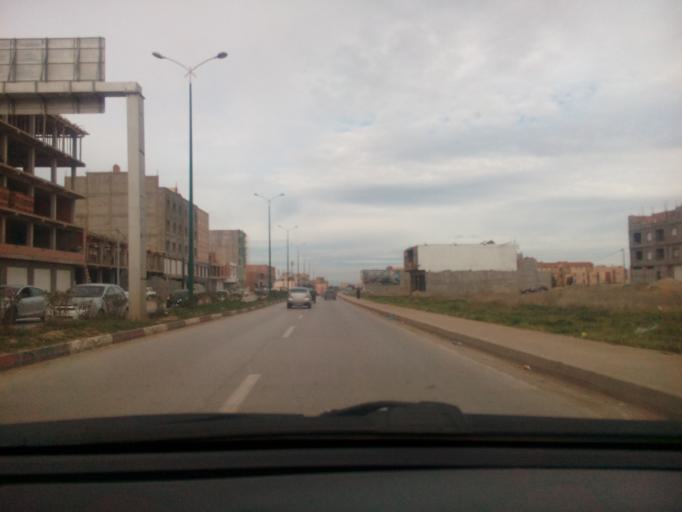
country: DZ
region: Tlemcen
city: Mansoura
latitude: 34.8854
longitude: -1.3524
